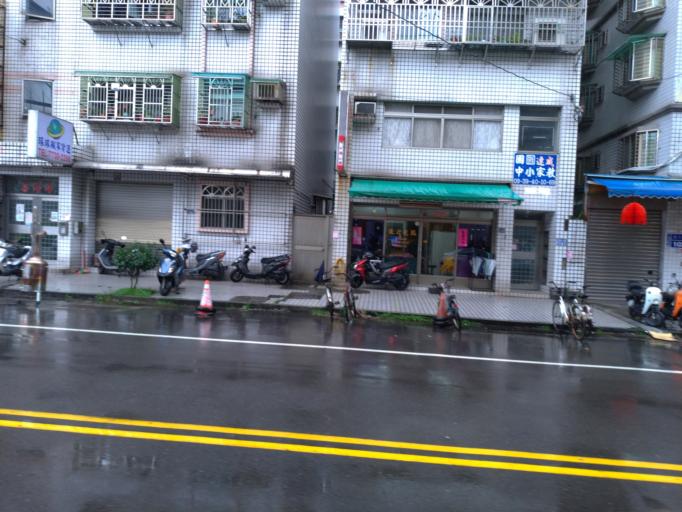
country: TW
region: Taiwan
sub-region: Keelung
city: Keelung
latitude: 25.0854
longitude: 121.6968
